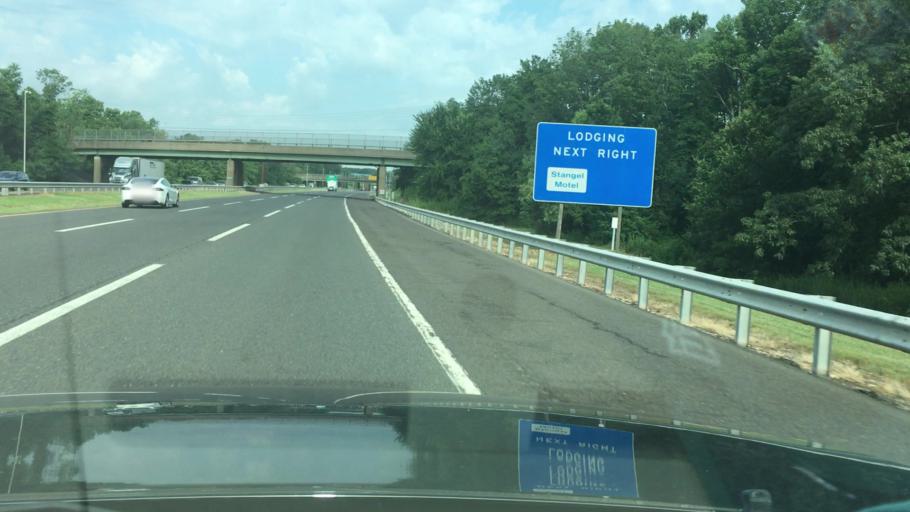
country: US
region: New Jersey
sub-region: Burlington County
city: Roebling
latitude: 40.0950
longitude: -74.7669
